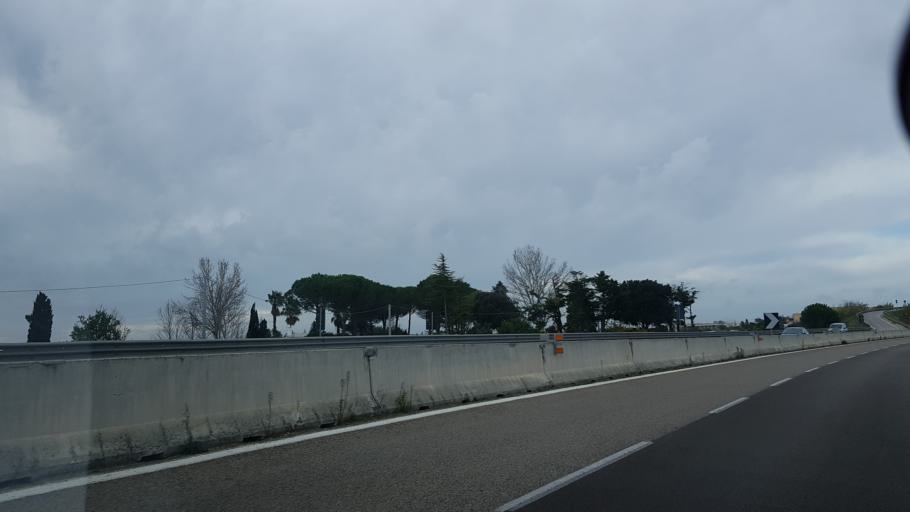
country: IT
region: Apulia
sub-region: Provincia di Brindisi
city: Mesagne
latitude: 40.5698
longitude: 17.8234
